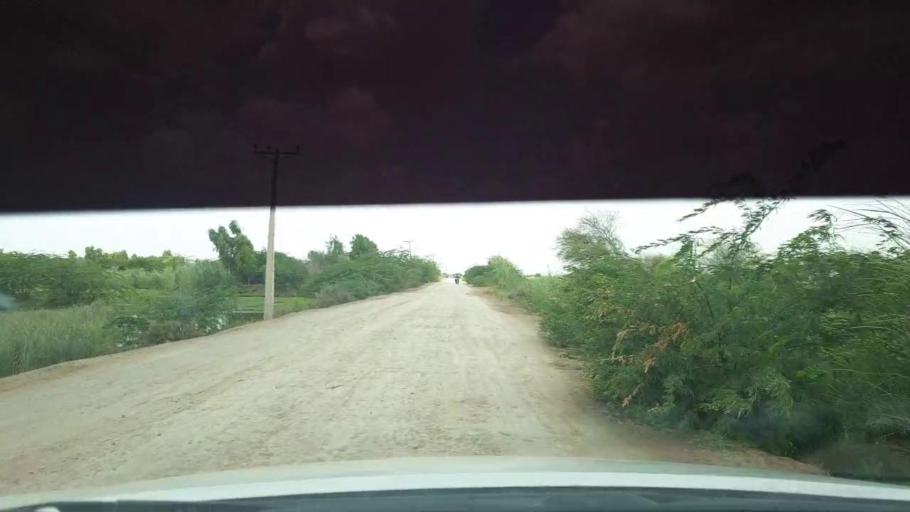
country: PK
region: Sindh
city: Kadhan
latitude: 24.4651
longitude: 68.9949
